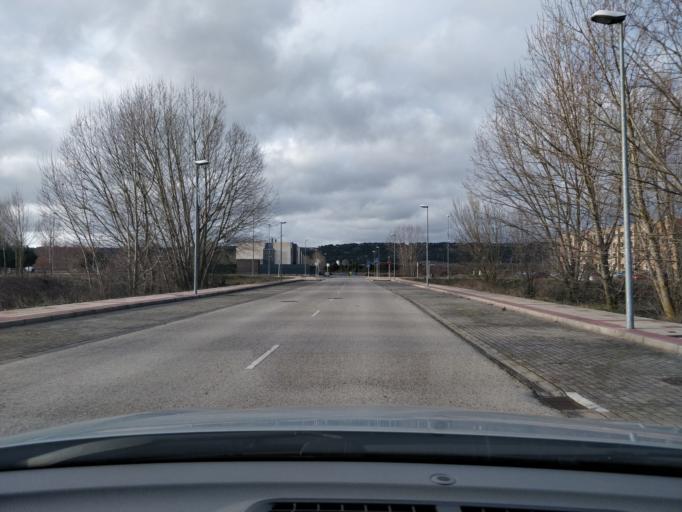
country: ES
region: Castille and Leon
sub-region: Provincia de Burgos
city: Villalbilla de Burgos
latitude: 42.3539
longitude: -3.7598
